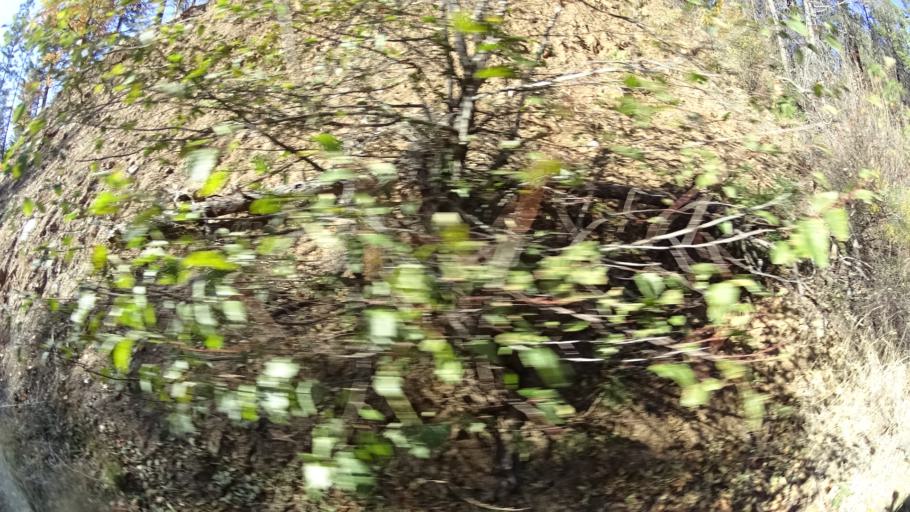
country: US
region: California
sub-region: Siskiyou County
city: Yreka
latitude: 41.8878
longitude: -122.8233
